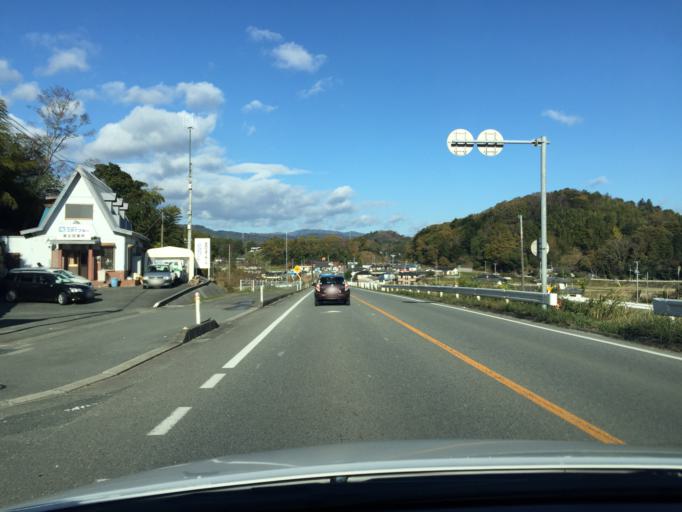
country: JP
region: Fukushima
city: Iwaki
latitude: 37.1995
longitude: 140.9952
